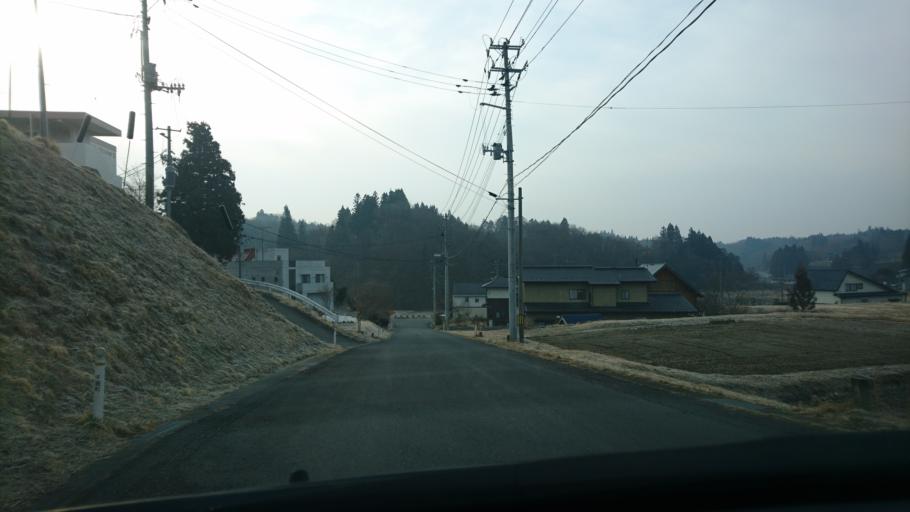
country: JP
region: Iwate
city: Ichinoseki
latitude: 38.9118
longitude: 141.3405
